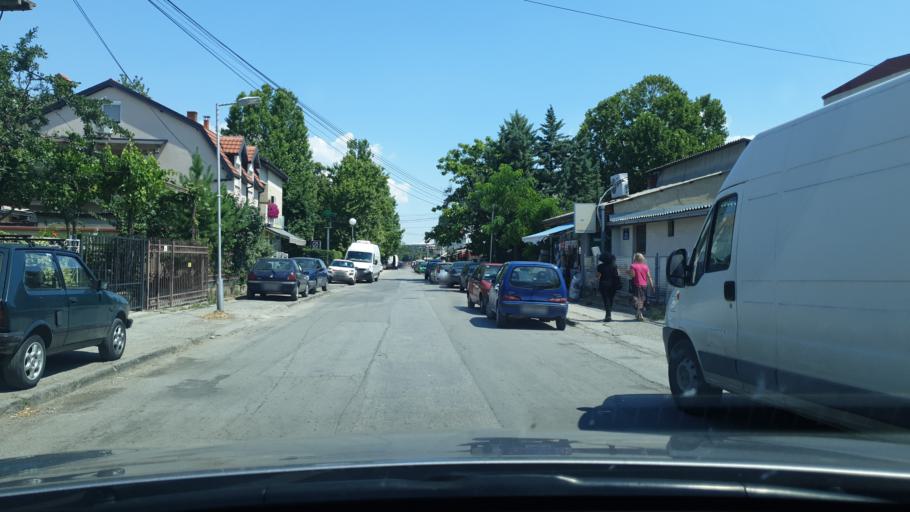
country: MK
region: Kisela Voda
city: Kisela Voda
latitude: 41.9381
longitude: 21.5149
